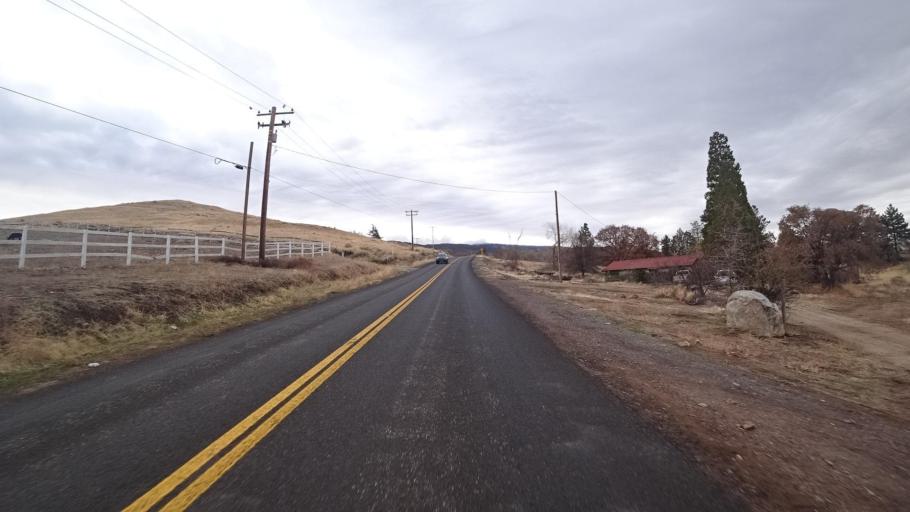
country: US
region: California
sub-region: Kern County
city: Golden Hills
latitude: 35.1065
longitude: -118.5250
